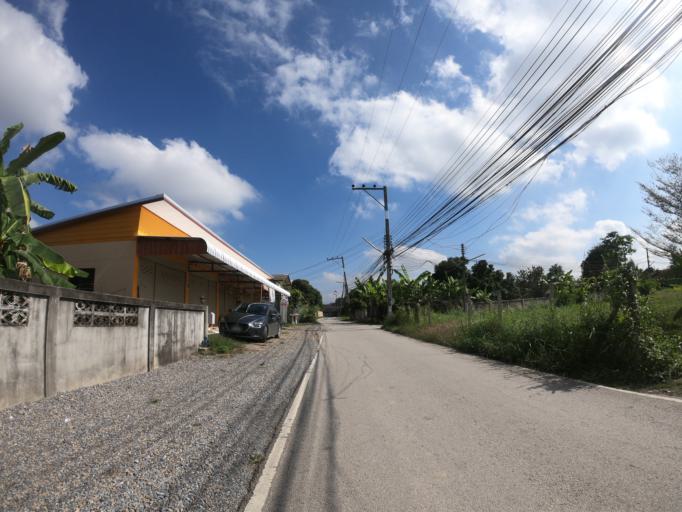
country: TH
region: Chiang Mai
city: Saraphi
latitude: 18.7209
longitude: 99.0210
